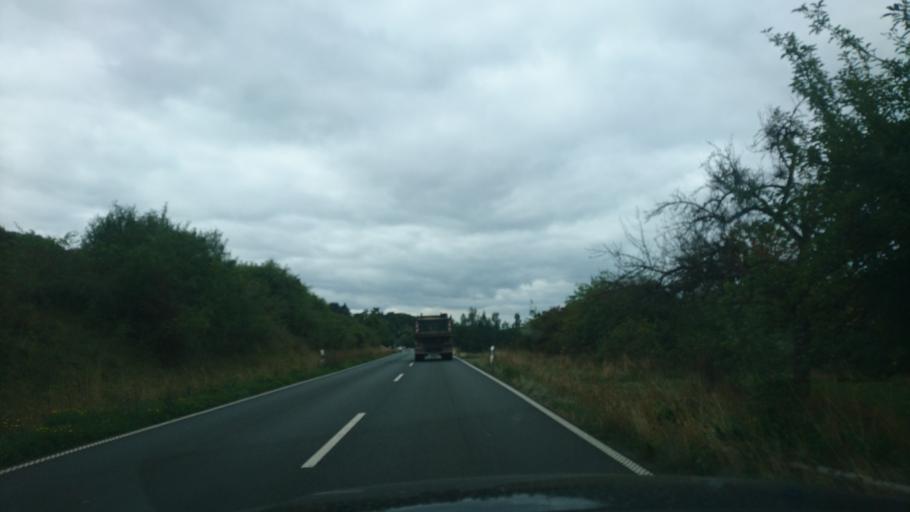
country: DE
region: Rheinland-Pfalz
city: Konz
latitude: 49.6904
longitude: 6.5898
